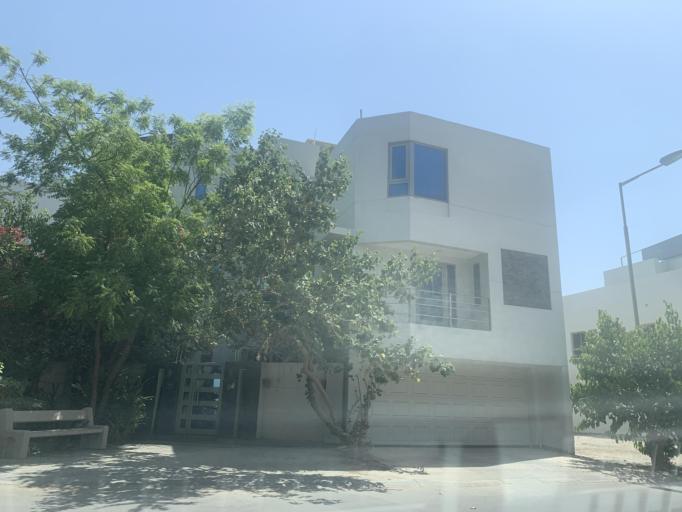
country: BH
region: Manama
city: Jidd Hafs
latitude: 26.2282
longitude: 50.5165
